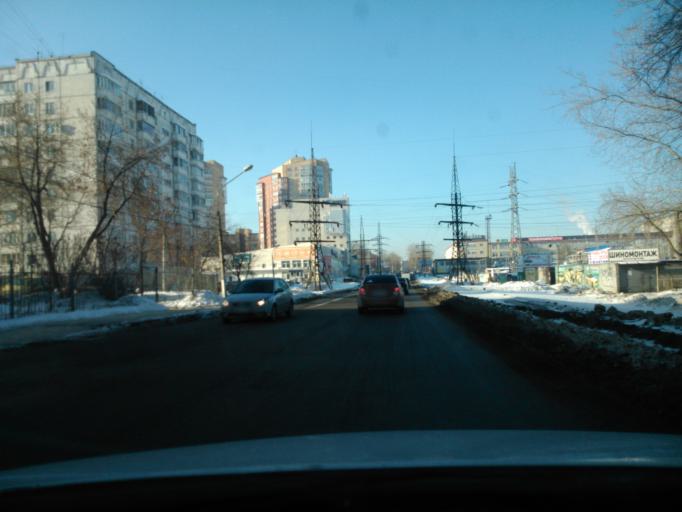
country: RU
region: Perm
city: Perm
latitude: 57.9871
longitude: 56.2122
